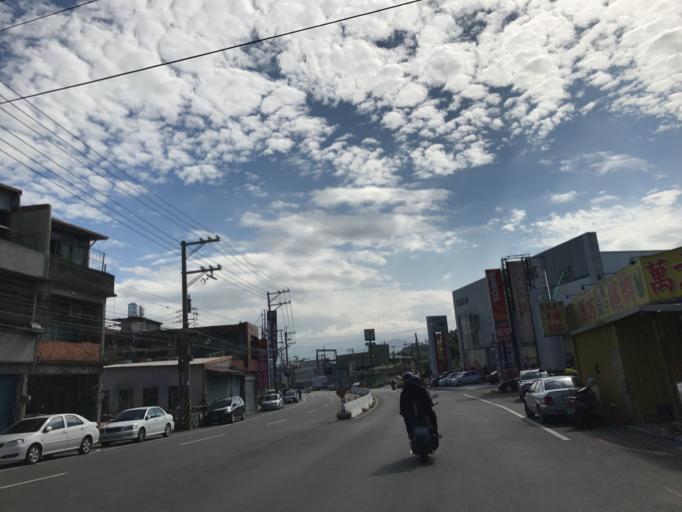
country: TW
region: Taiwan
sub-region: Hsinchu
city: Zhubei
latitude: 24.7553
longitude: 121.0709
